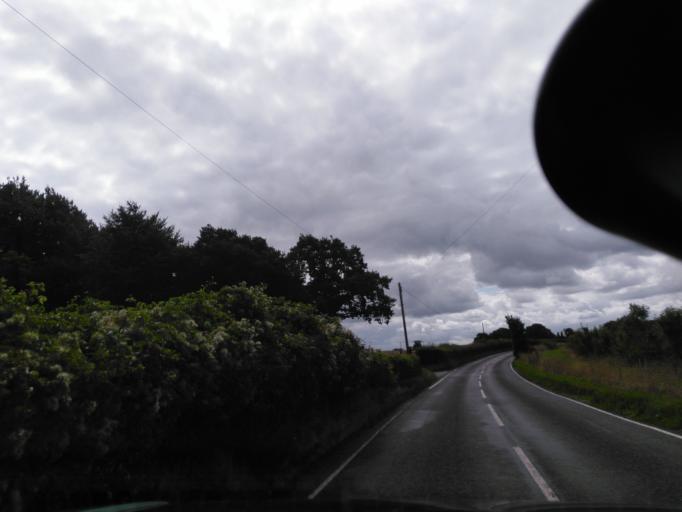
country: GB
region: England
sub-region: Dorset
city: Blandford Forum
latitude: 50.9018
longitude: -2.1556
